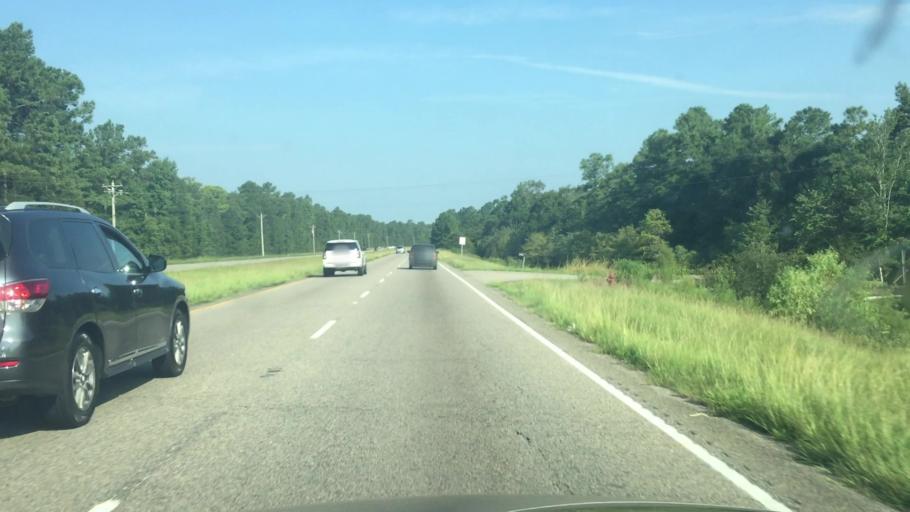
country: US
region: South Carolina
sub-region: Horry County
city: North Myrtle Beach
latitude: 33.9130
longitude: -78.7160
